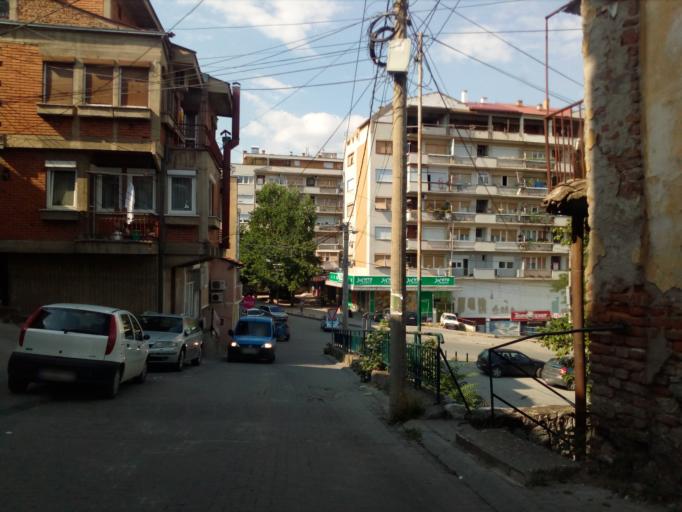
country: MK
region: Veles
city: Veles
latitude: 41.7143
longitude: 21.7837
